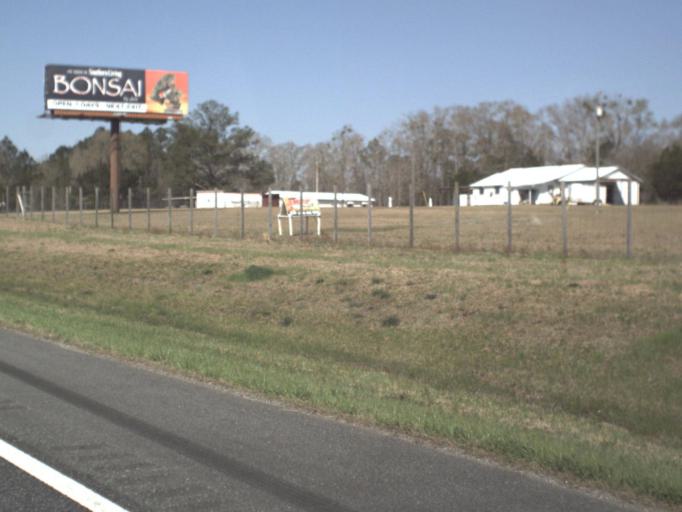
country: US
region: Florida
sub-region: Jackson County
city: Marianna
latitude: 30.7578
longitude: -85.2908
